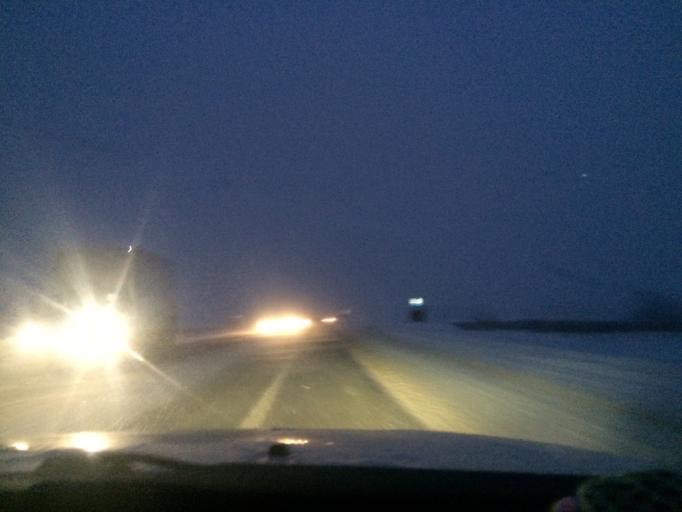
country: RU
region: Tula
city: Kosaya Gora
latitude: 54.1574
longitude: 37.5074
